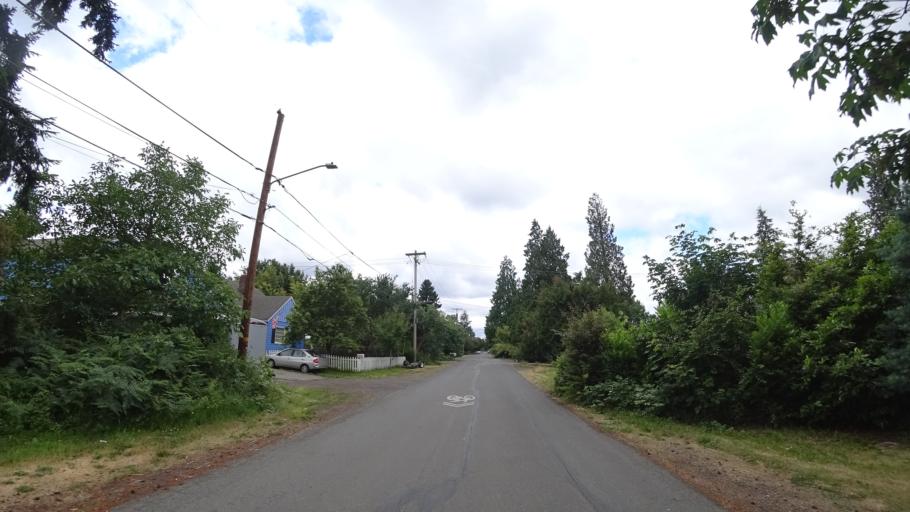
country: US
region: Oregon
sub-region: Multnomah County
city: Lents
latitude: 45.5591
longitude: -122.5925
